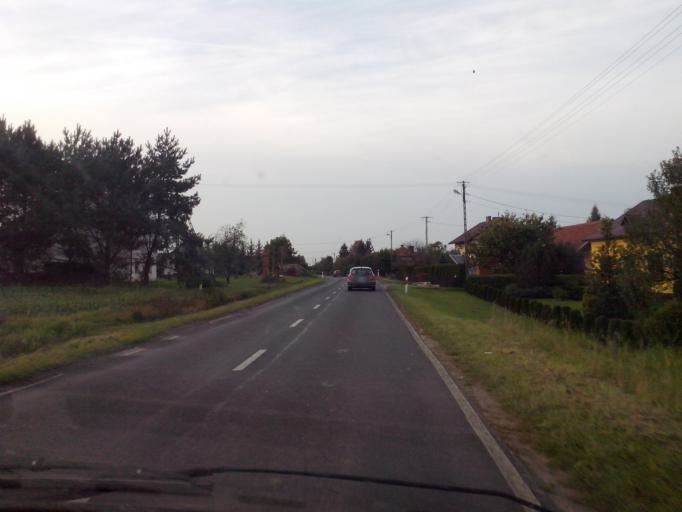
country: PL
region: Subcarpathian Voivodeship
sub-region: Powiat strzyzowski
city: Strzyzow
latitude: 49.8379
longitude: 21.8233
